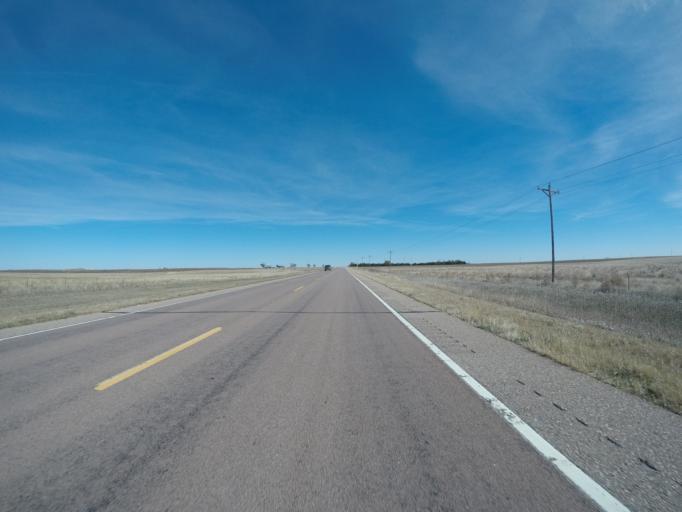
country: US
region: Colorado
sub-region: Yuma County
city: Yuma
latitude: 39.6560
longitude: -102.6340
